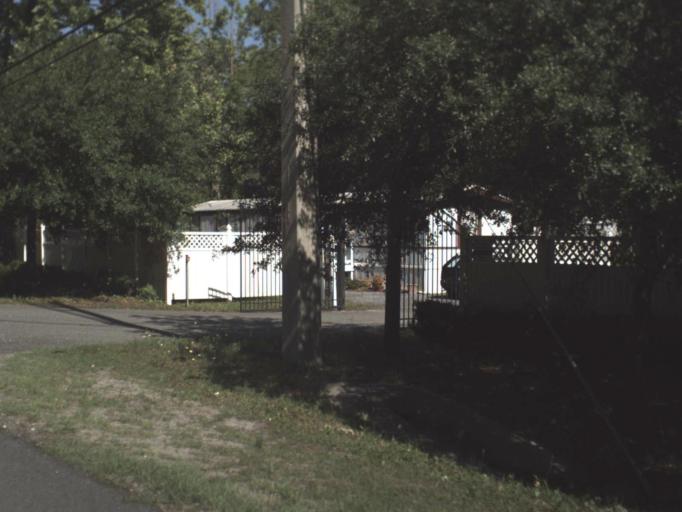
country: US
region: Florida
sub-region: Duval County
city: Jacksonville
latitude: 30.3228
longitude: -81.7742
